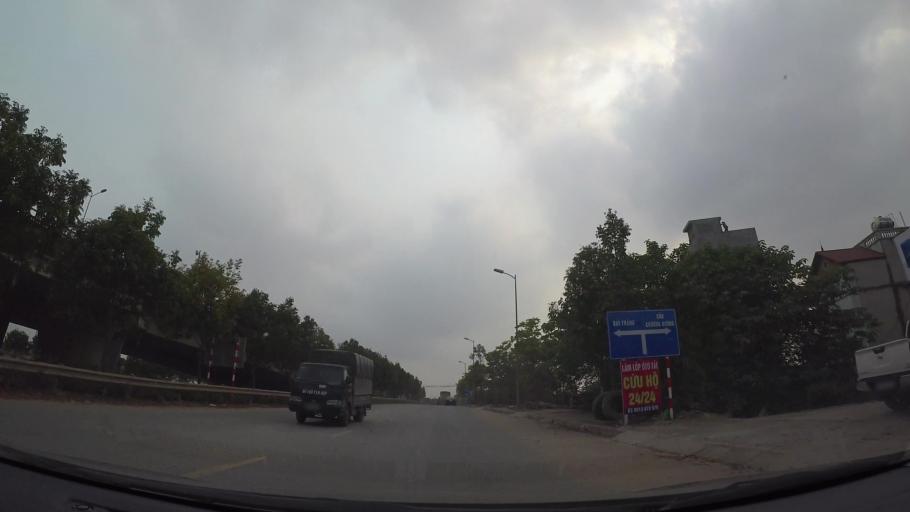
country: VN
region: Ha Noi
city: Trau Quy
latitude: 21.0038
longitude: 105.9104
